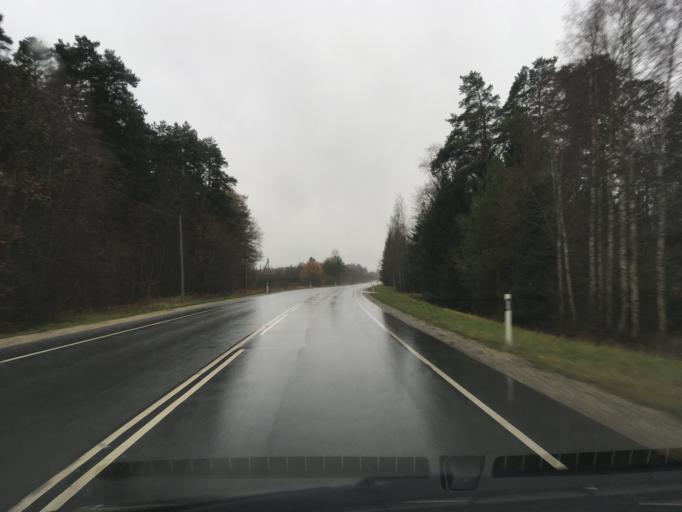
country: EE
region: Harju
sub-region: Nissi vald
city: Turba
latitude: 58.8990
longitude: 24.1069
